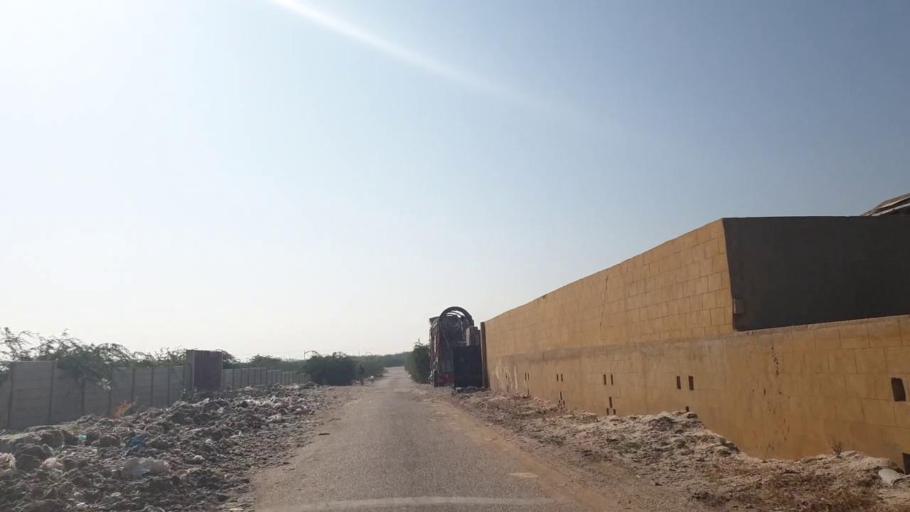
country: PK
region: Sindh
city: Thatta
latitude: 25.1546
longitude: 67.7738
